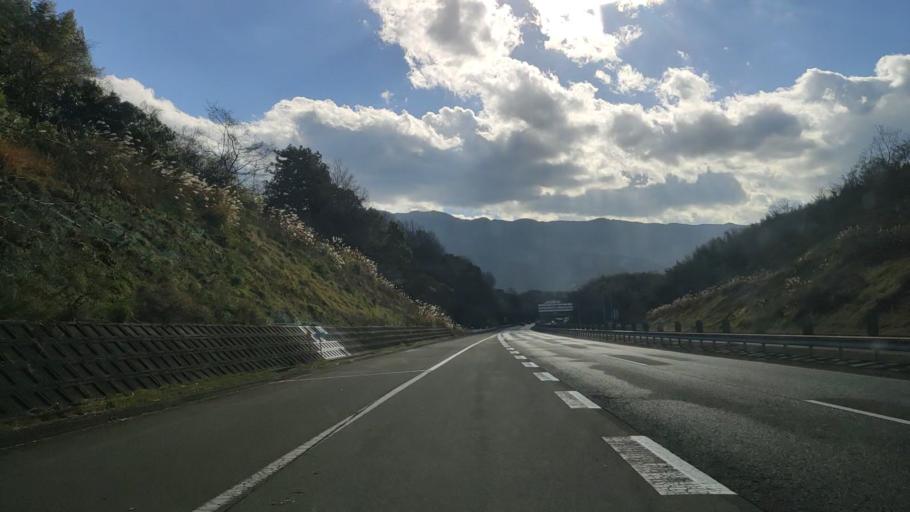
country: JP
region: Ehime
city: Kawanoecho
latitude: 33.9975
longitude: 133.5964
